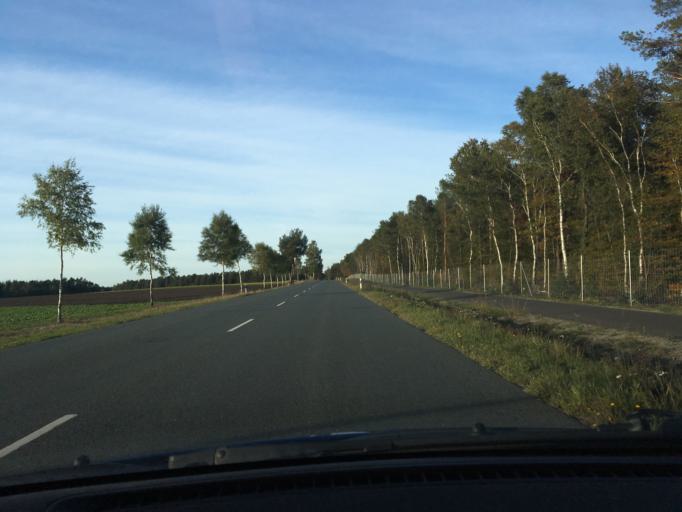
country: DE
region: Lower Saxony
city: Munster
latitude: 53.0360
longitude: 10.0593
